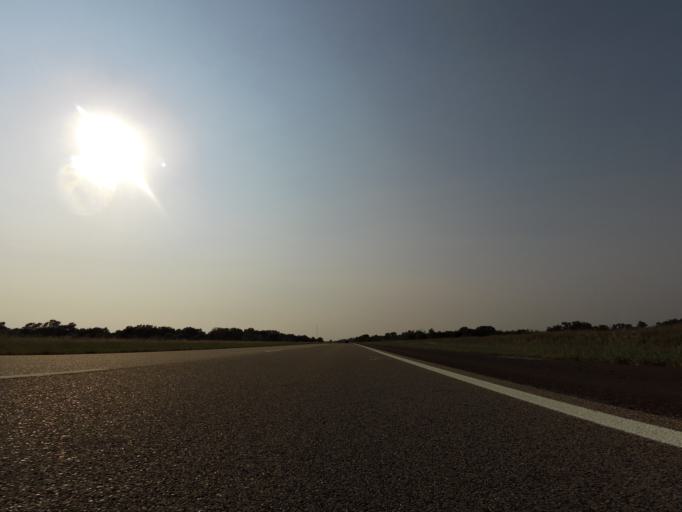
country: US
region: Kansas
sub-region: Reno County
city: South Hutchinson
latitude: 37.9620
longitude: -97.9163
